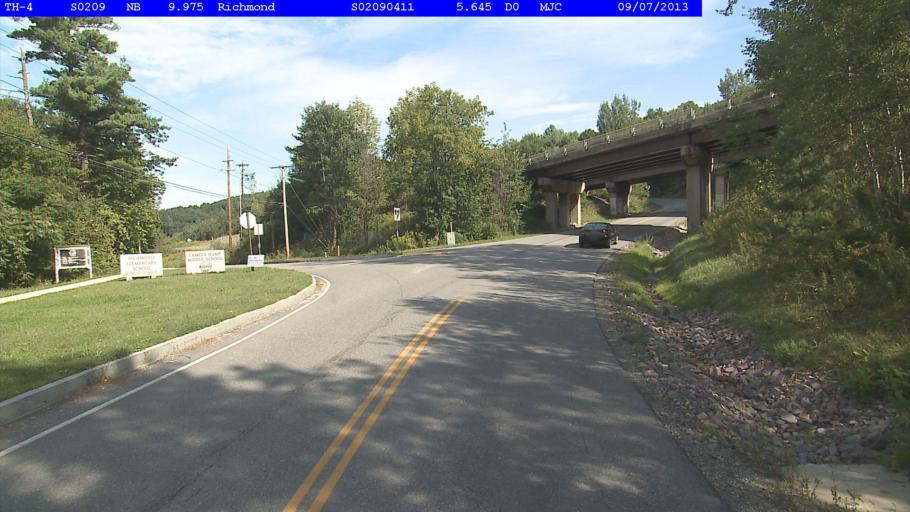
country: US
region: Vermont
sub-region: Chittenden County
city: Williston
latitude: 44.4113
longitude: -72.9917
